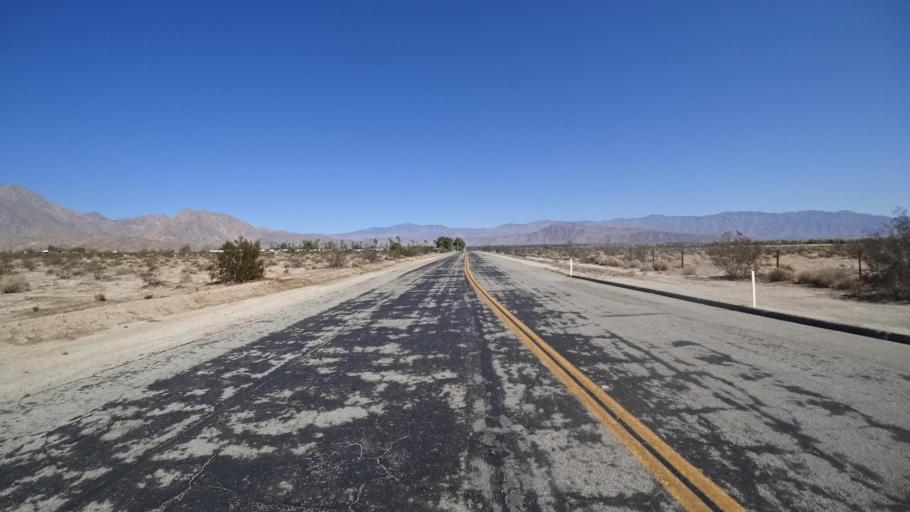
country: US
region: California
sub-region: San Diego County
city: Borrego Springs
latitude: 33.2318
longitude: -116.3656
